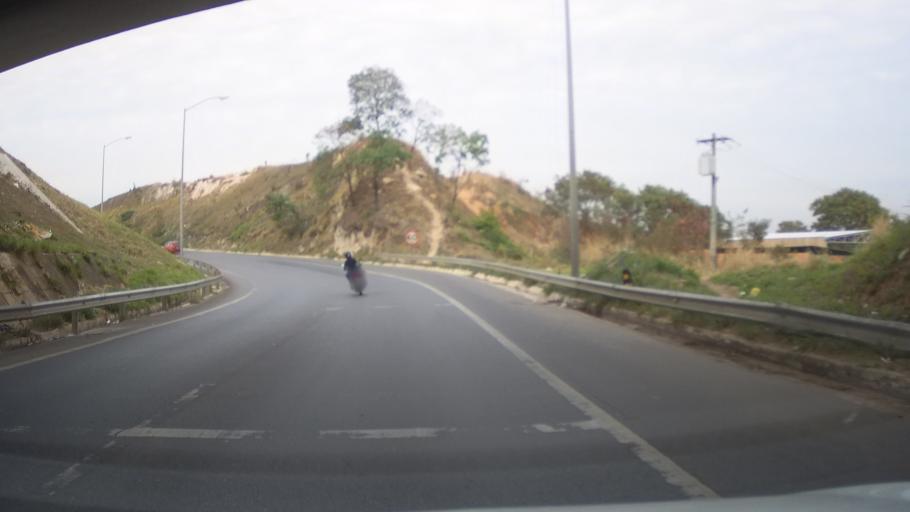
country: BR
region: Minas Gerais
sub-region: Vespasiano
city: Vespasiano
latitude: -19.7605
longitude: -43.9482
